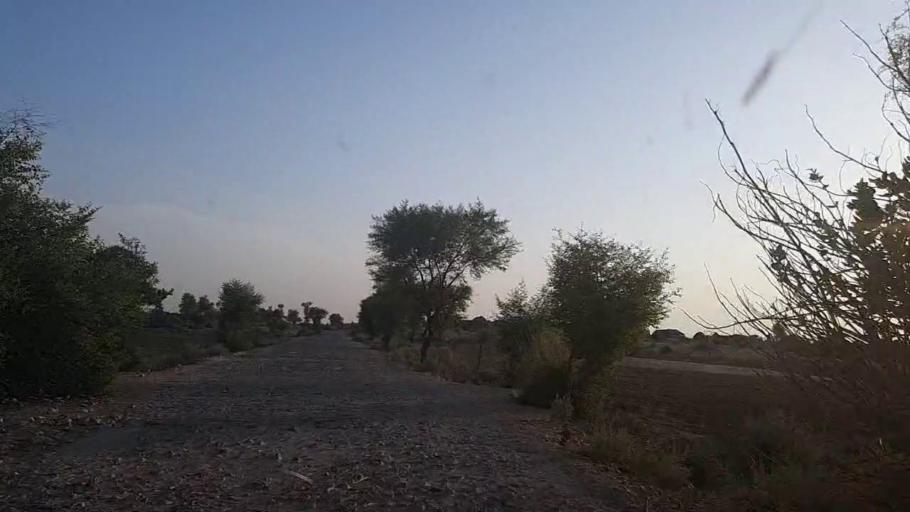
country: PK
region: Sindh
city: Khanpur
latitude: 27.6316
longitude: 69.4465
